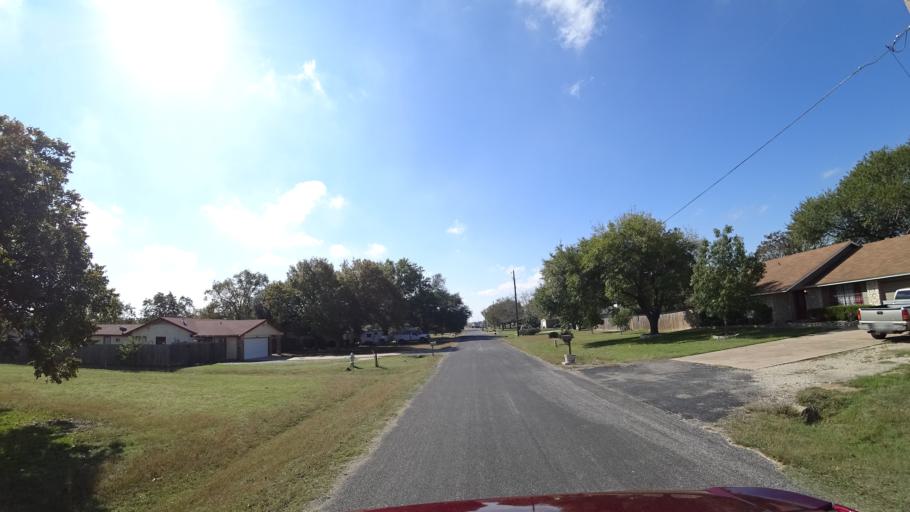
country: US
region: Texas
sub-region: Travis County
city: Windemere
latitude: 30.4407
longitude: -97.6542
